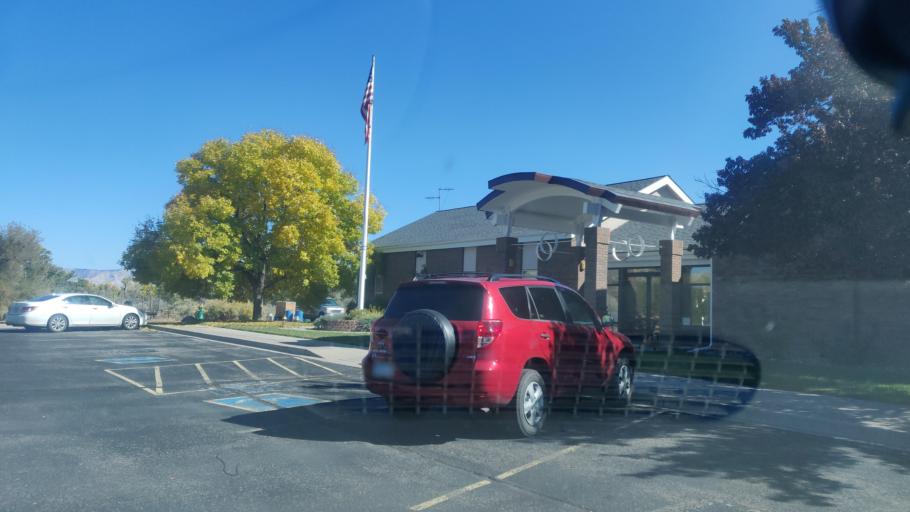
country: US
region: Colorado
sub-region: Mesa County
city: Redlands
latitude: 39.0701
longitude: -108.6436
